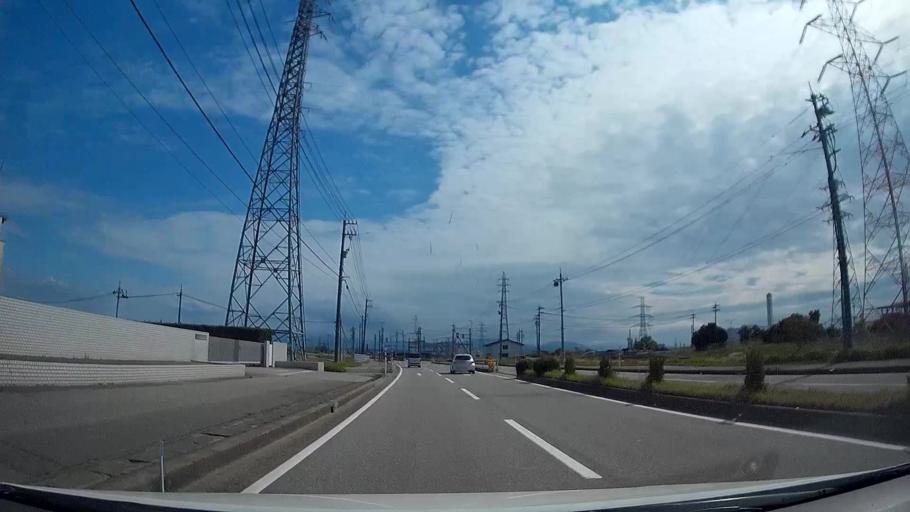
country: JP
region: Toyama
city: Kuragaki-kosugi
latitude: 36.7484
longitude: 137.1296
